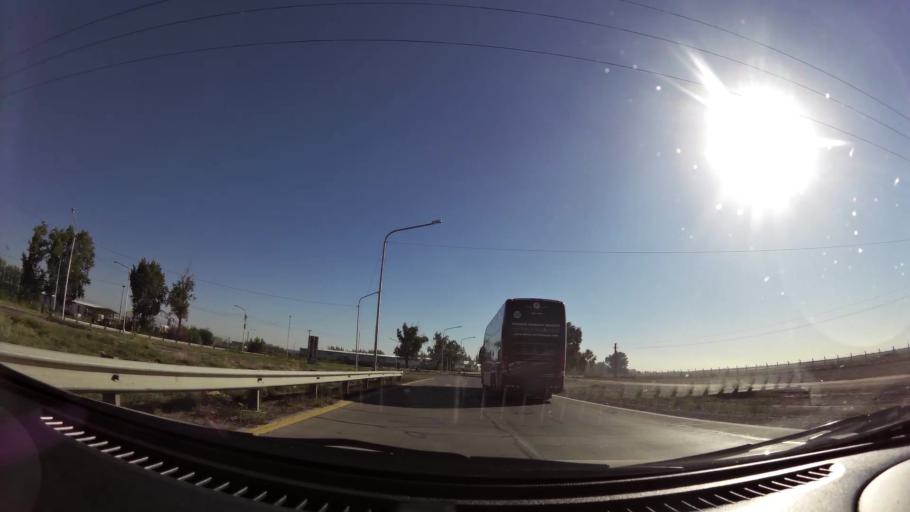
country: AR
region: Mendoza
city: Las Heras
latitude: -32.8218
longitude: -68.8026
